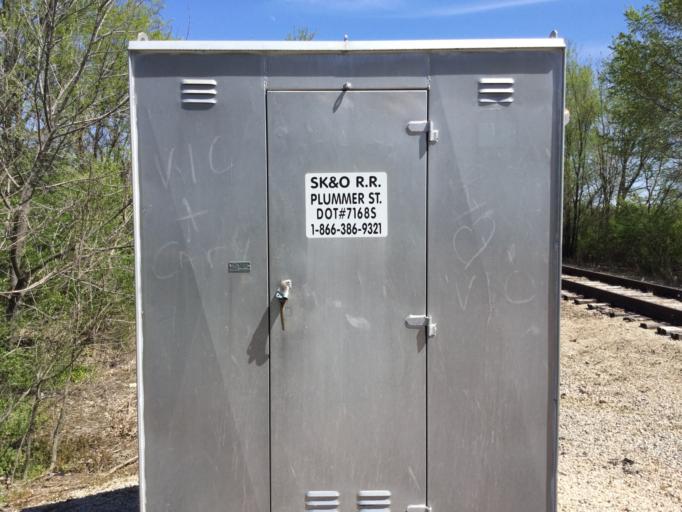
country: US
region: Kansas
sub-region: Neosho County
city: Chanute
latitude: 37.6633
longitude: -95.4710
